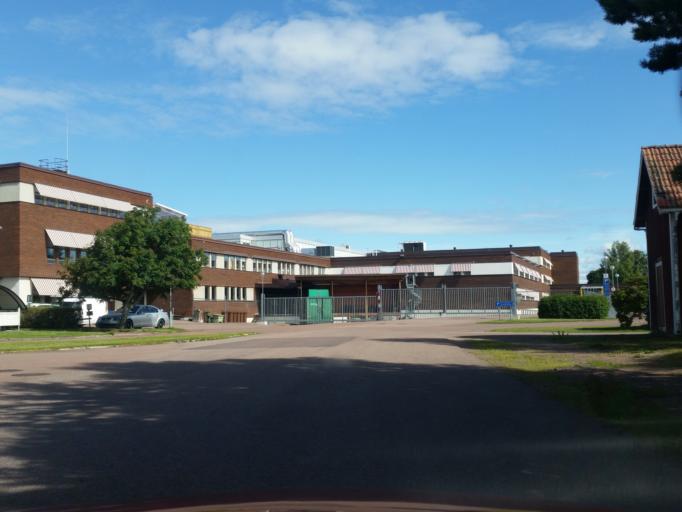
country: SE
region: Dalarna
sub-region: Leksand Municipality
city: Smedby
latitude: 60.6727
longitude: 15.0899
